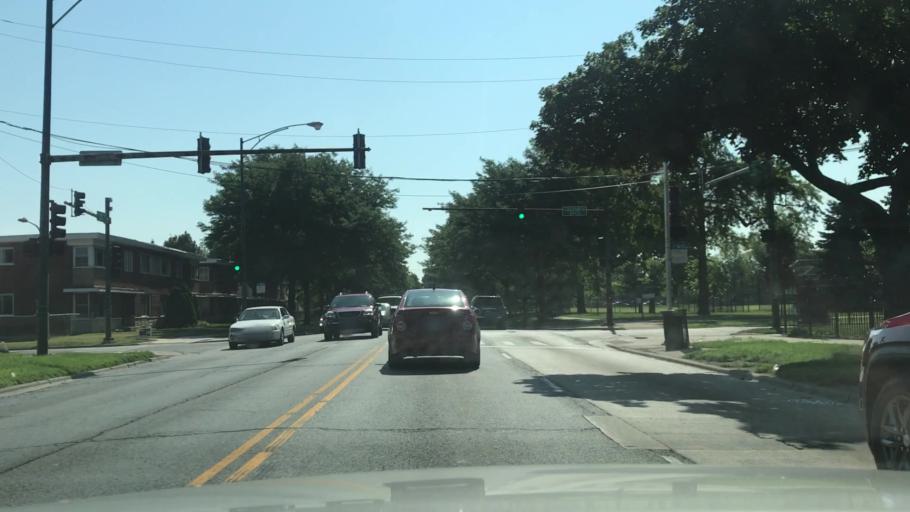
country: US
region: Illinois
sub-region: Cook County
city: Burnham
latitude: 41.7081
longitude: -87.5661
